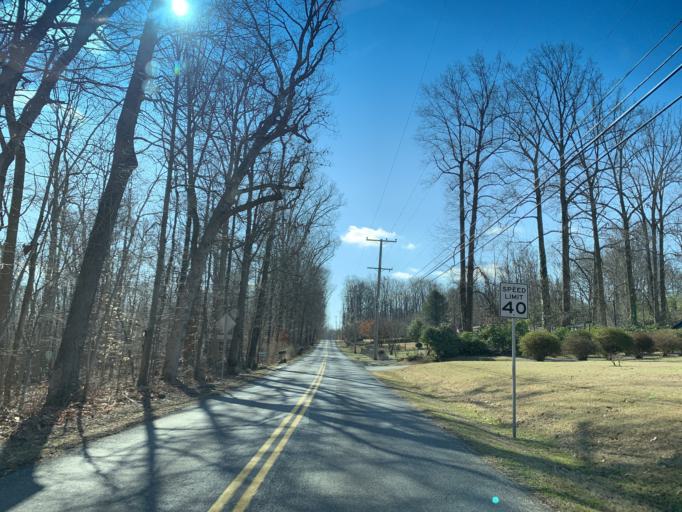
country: US
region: Maryland
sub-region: Harford County
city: Riverside
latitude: 39.5107
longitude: -76.2359
